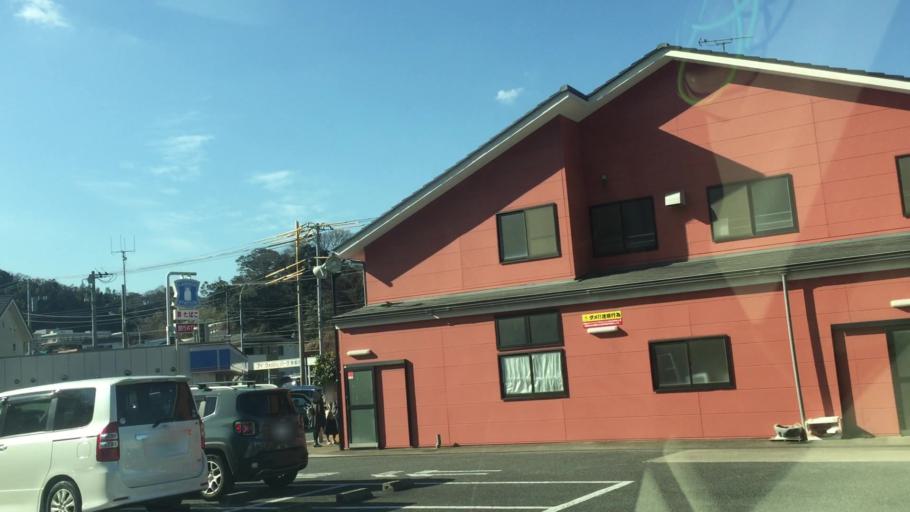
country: JP
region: Kanagawa
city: Zushi
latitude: 35.3654
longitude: 139.6124
